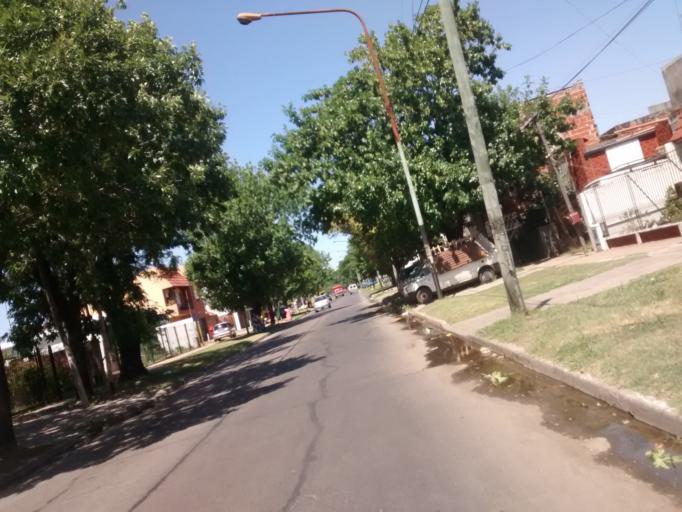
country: AR
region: Buenos Aires
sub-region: Partido de La Plata
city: La Plata
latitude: -34.9328
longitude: -57.9148
